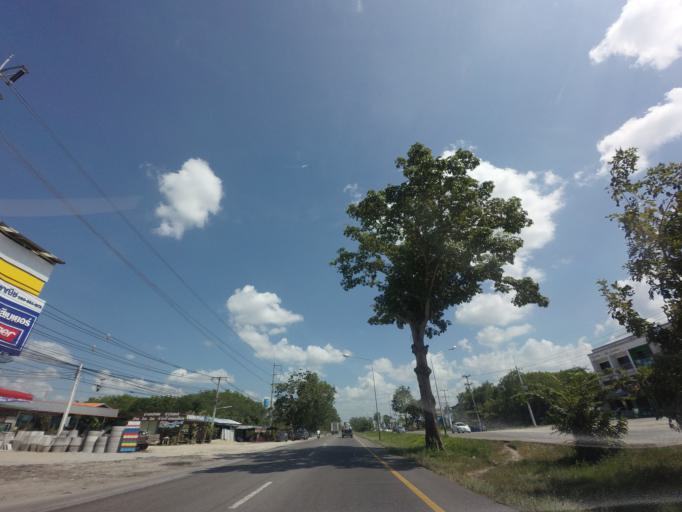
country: TH
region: Chon Buri
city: Ban Bueng
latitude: 13.3016
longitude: 101.1441
